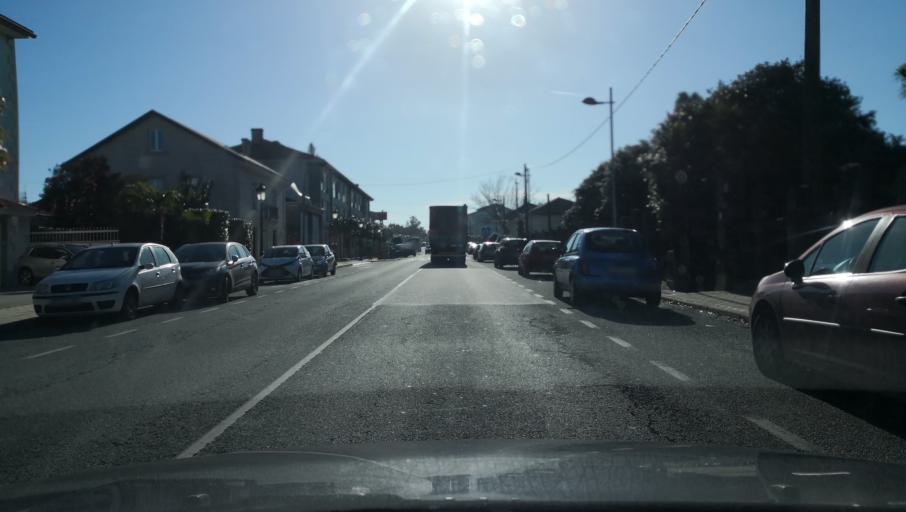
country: ES
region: Galicia
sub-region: Provincia da Coruna
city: Vedra
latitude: 42.7976
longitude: -8.4699
